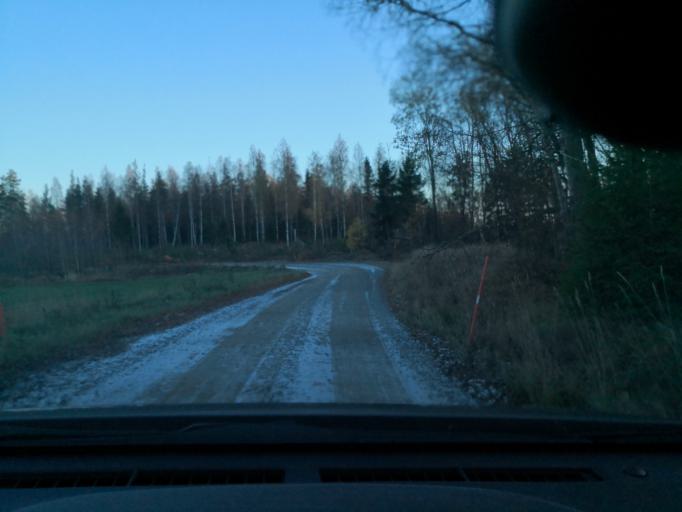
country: SE
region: Vaestmanland
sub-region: Vasteras
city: Tillberga
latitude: 59.7679
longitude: 16.6034
